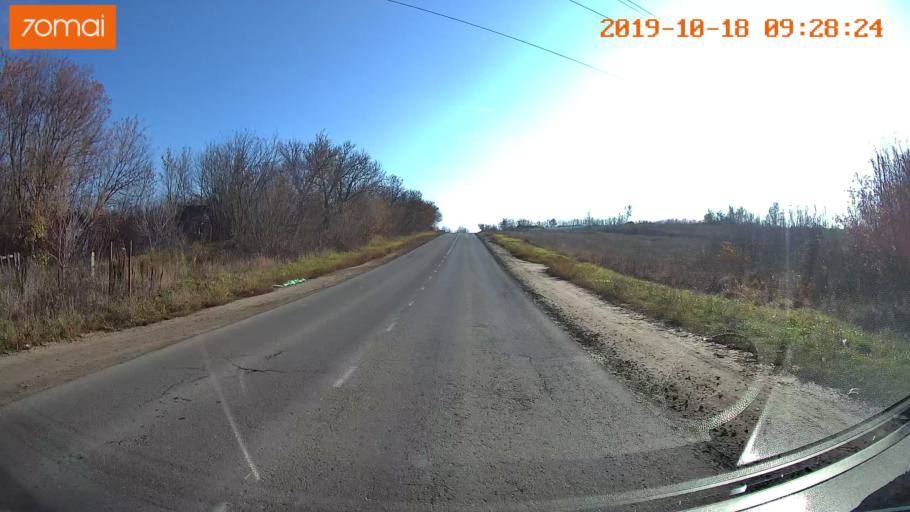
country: RU
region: Tula
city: Yefremov
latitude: 53.1339
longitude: 38.1363
